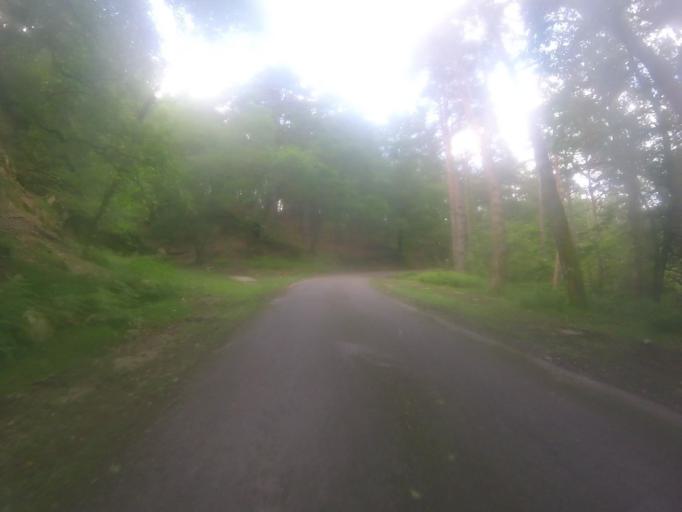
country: ES
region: Navarre
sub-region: Provincia de Navarra
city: Arantza
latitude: 43.2253
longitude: -1.8011
